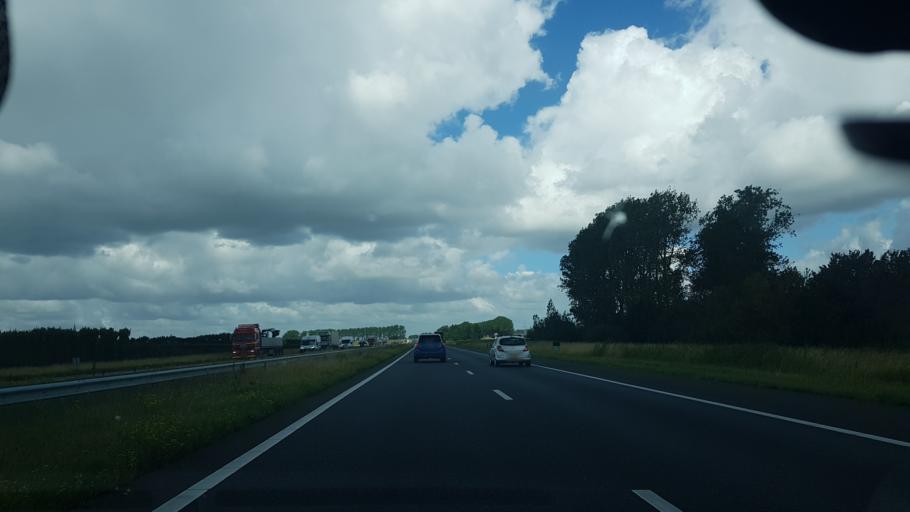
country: NL
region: Zeeland
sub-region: Gemeente Reimerswaal
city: Yerseke
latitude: 51.4467
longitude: 4.0503
